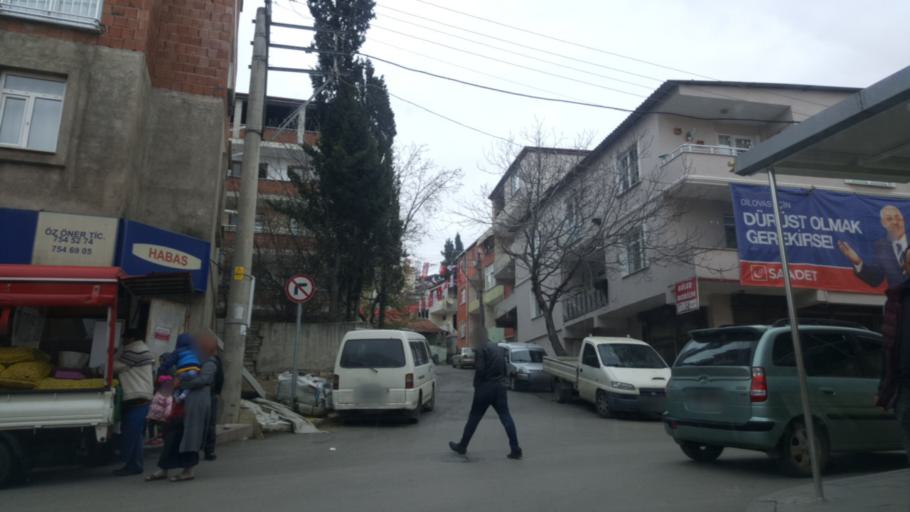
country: TR
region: Kocaeli
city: Tavsancil
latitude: 40.7856
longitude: 29.5430
